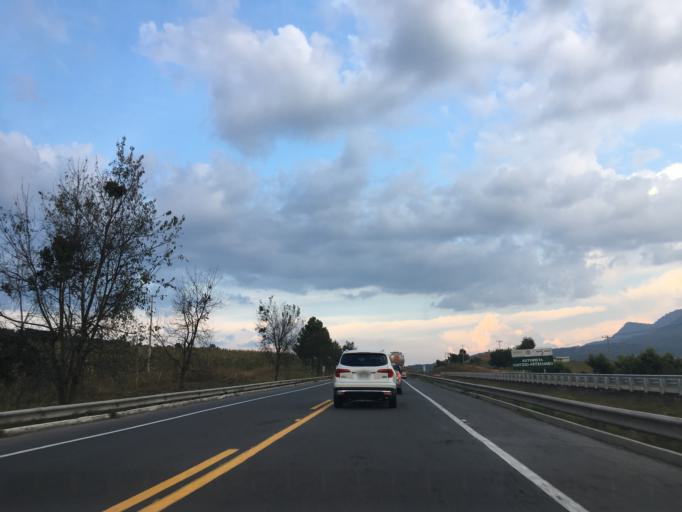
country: MX
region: Michoacan
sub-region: Patzcuaro
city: Colonia Vista Bella (Lomas del Peaje)
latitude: 19.5017
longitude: -101.5837
